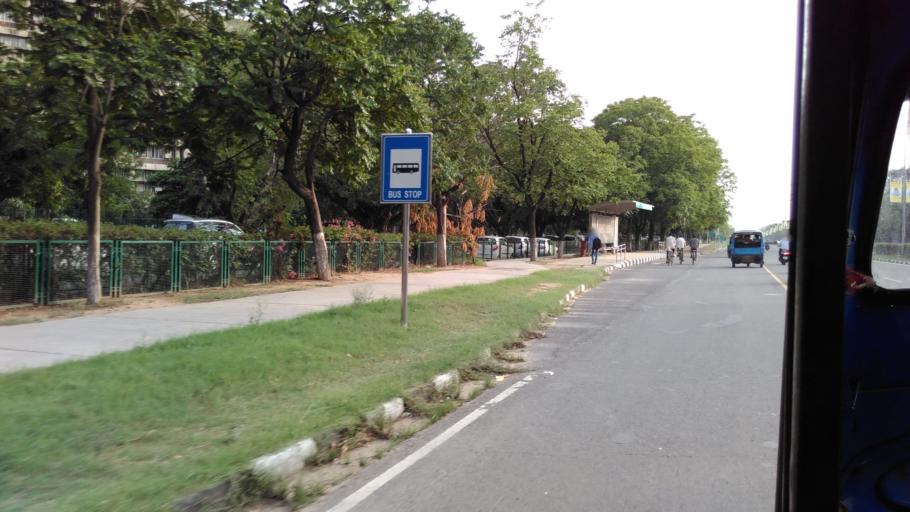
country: IN
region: Chandigarh
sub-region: Chandigarh
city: Chandigarh
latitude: 30.7493
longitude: 76.7901
